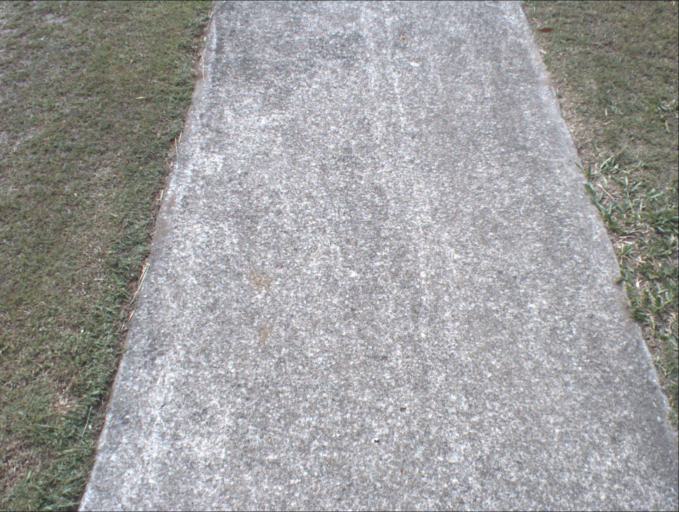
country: AU
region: Queensland
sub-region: Logan
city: Rochedale South
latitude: -27.5949
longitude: 153.1241
